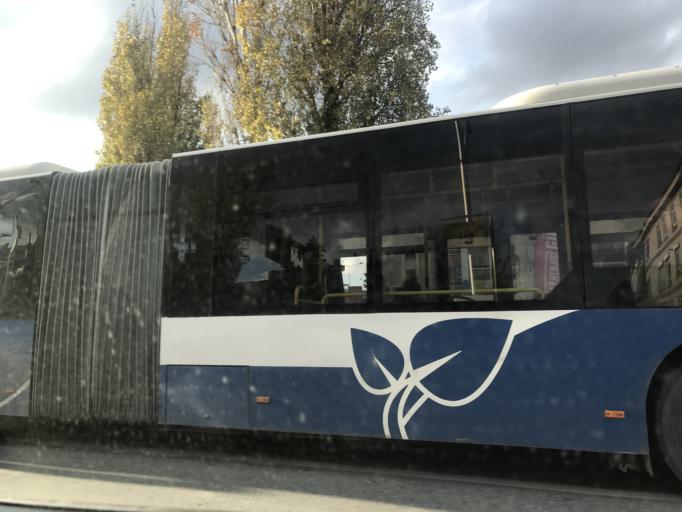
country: TR
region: Ankara
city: Mamak
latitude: 39.9644
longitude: 32.8713
